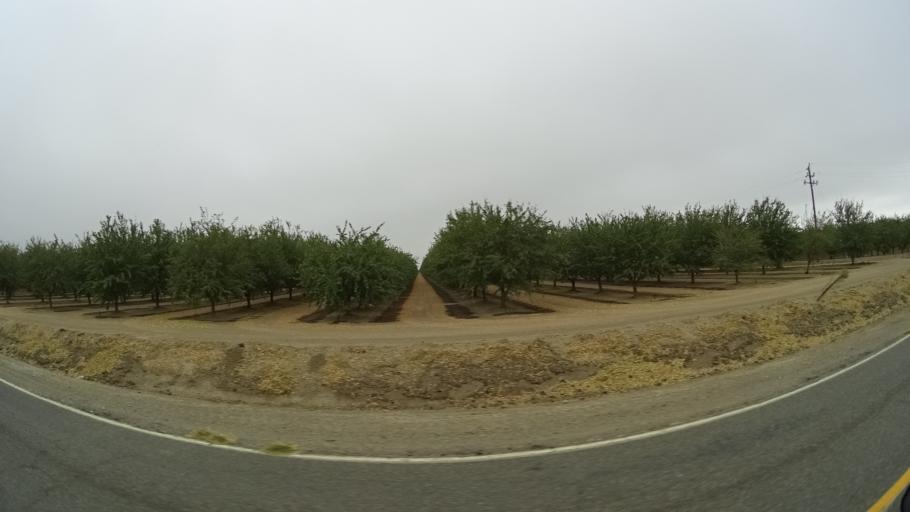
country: US
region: California
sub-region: Yolo County
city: Dunnigan
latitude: 38.9257
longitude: -122.0125
